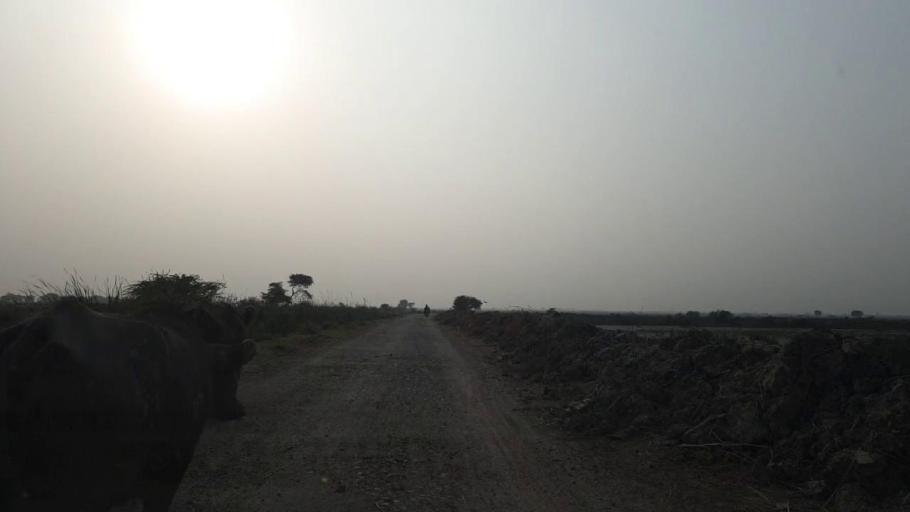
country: PK
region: Sindh
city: Mirpur Batoro
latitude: 24.6544
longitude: 68.3801
